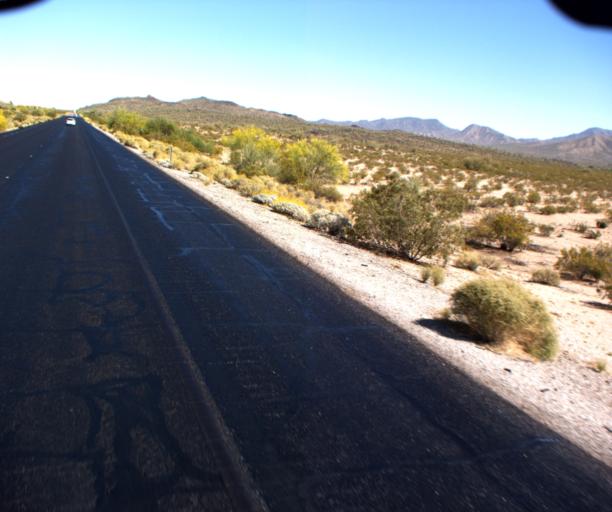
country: US
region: Arizona
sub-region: Pinal County
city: Maricopa
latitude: 32.8365
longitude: -112.2086
